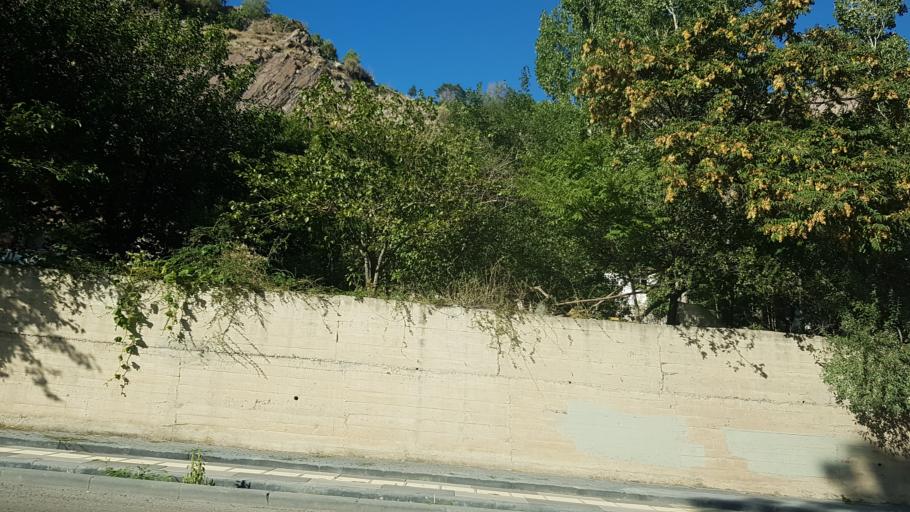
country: TR
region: Ankara
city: Cankaya
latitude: 39.9433
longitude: 32.8668
